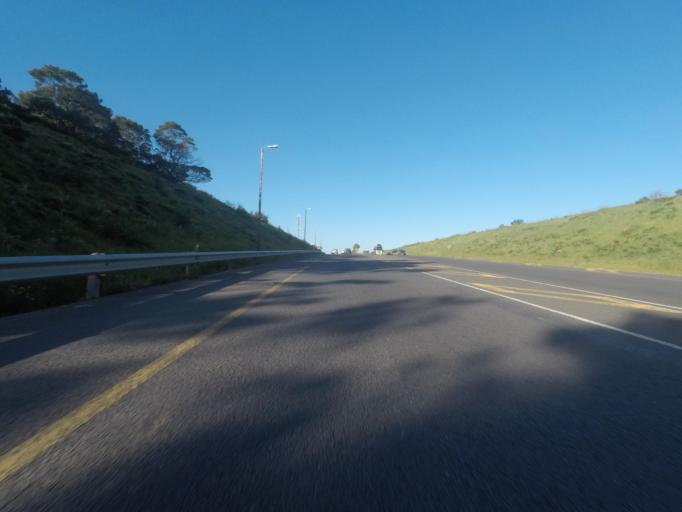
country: ZA
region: Eastern Cape
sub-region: Buffalo City Metropolitan Municipality
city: East London
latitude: -33.0413
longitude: 27.8302
